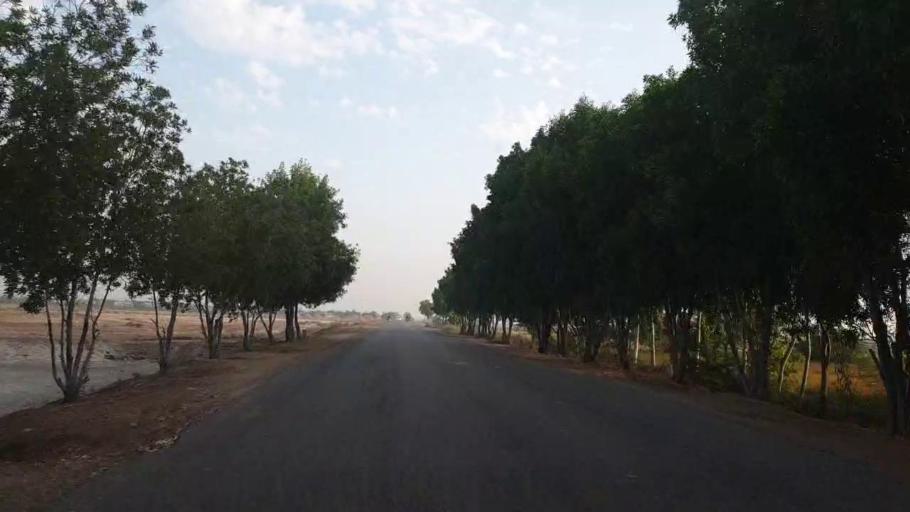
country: PK
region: Sindh
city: Badin
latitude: 24.6852
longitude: 68.9129
